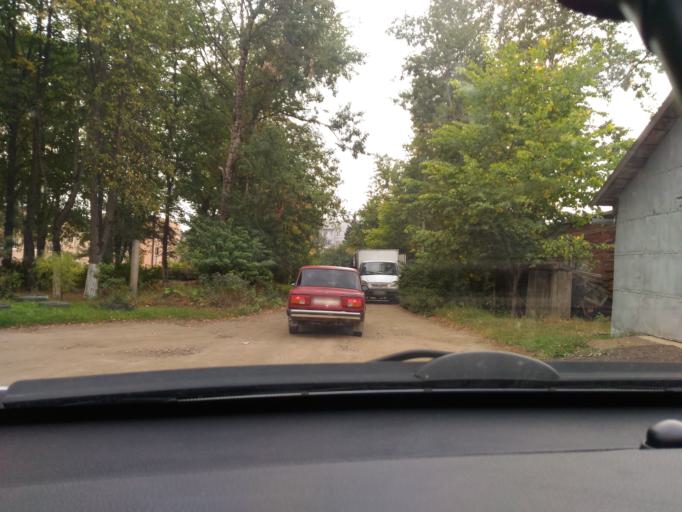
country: RU
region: Moskovskaya
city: Povarovo
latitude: 56.0902
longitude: 37.0623
